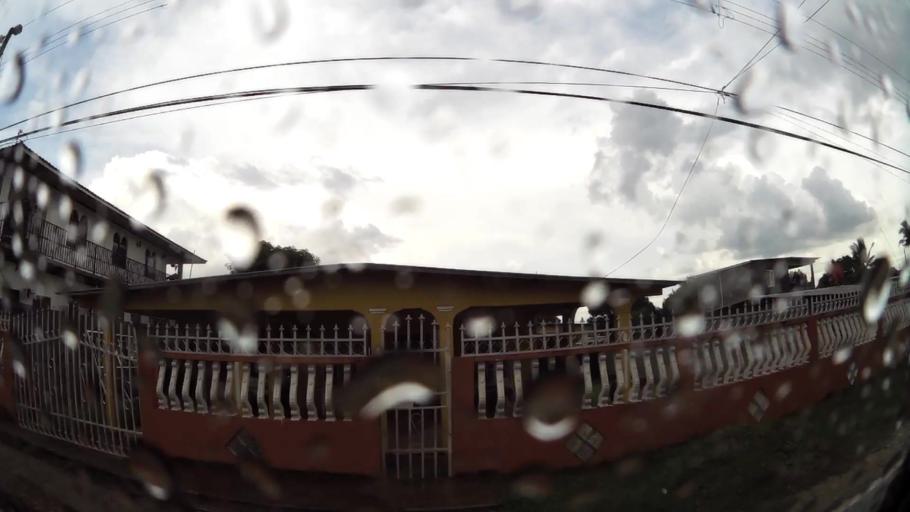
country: PA
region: Panama
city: Cabra Numero Uno
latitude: 9.1012
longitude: -79.3283
